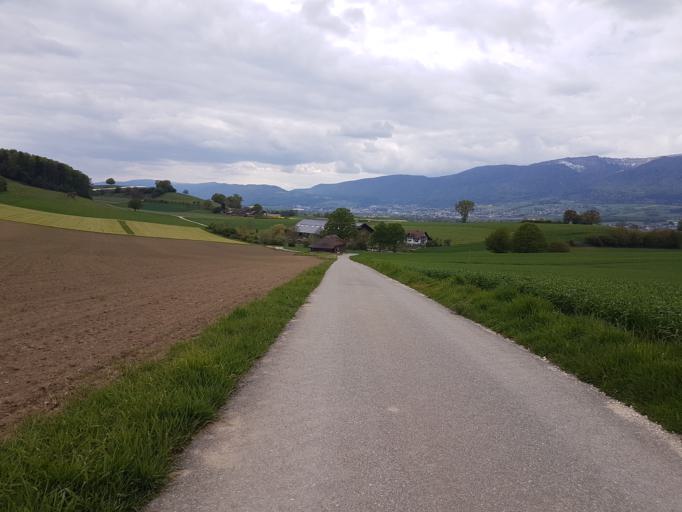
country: CH
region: Bern
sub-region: Seeland District
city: Leuzigen
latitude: 47.1806
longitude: 7.4889
